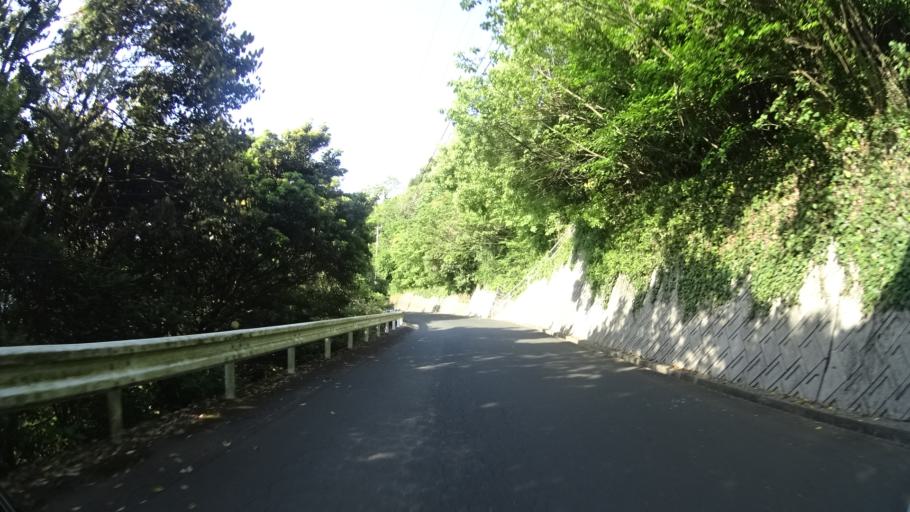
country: JP
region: Ehime
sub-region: Nishiuwa-gun
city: Ikata-cho
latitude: 33.3755
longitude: 132.0621
